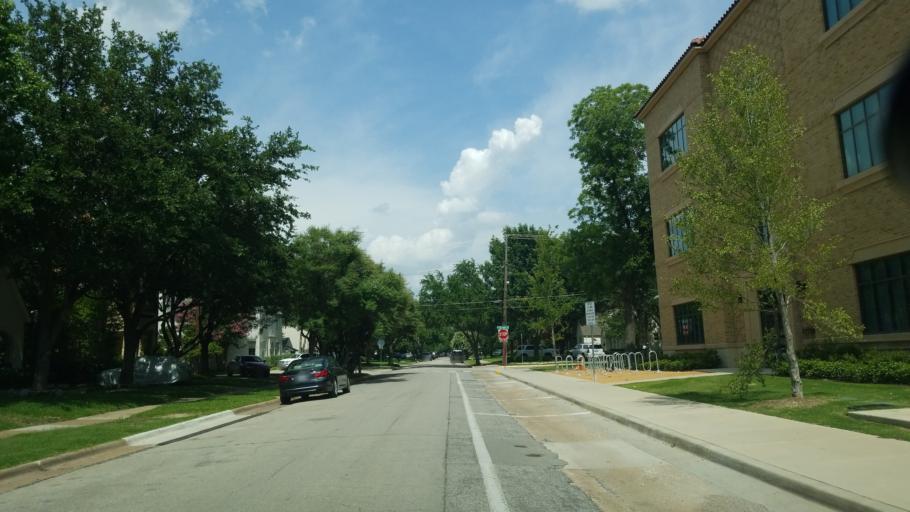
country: US
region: Texas
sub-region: Dallas County
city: University Park
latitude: 32.8521
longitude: -96.7908
